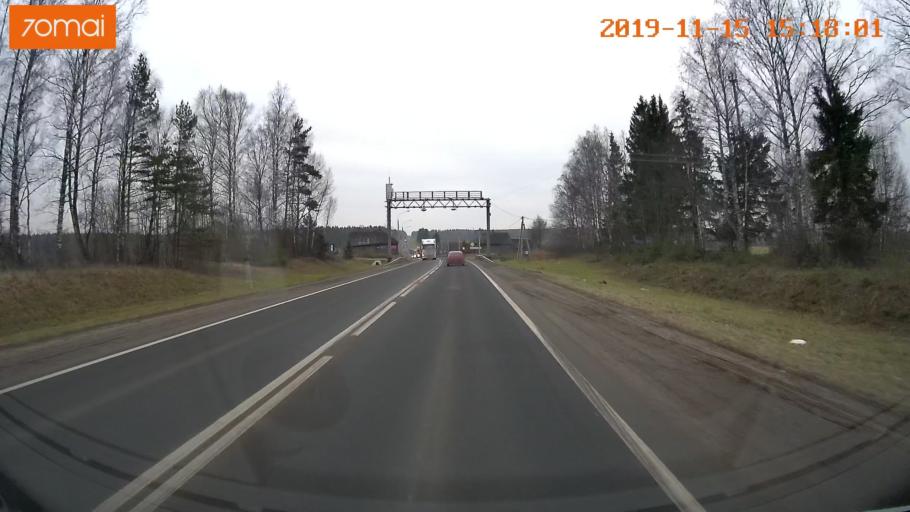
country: RU
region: Jaroslavl
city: Danilov
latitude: 58.2529
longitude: 40.1806
